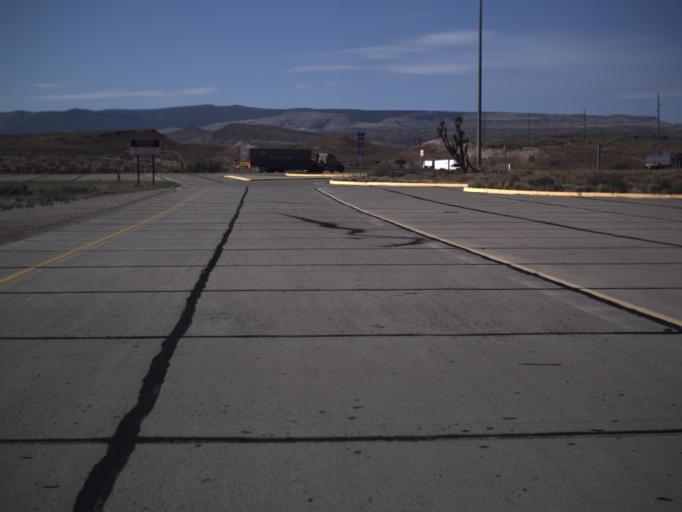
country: US
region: Utah
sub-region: Washington County
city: Saint George
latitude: 37.0121
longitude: -113.6134
